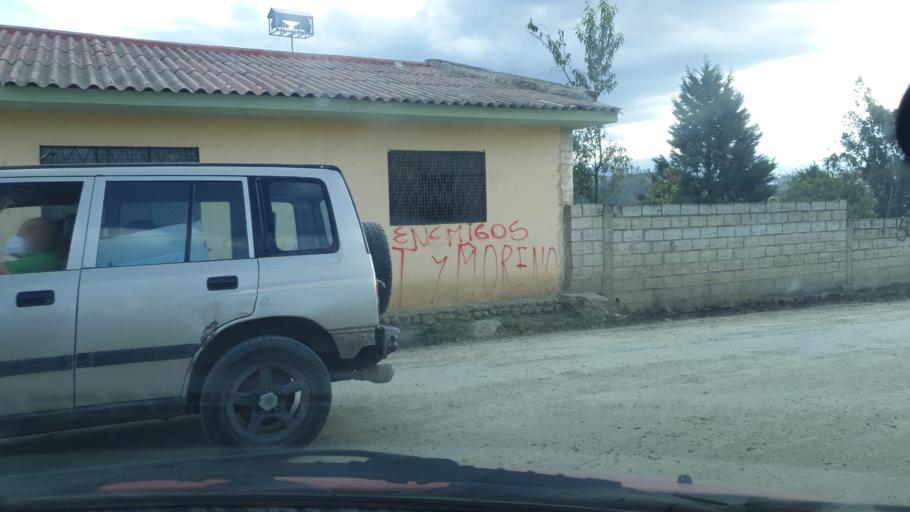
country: EC
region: Azuay
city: Cuenca
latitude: -2.9251
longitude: -78.9730
